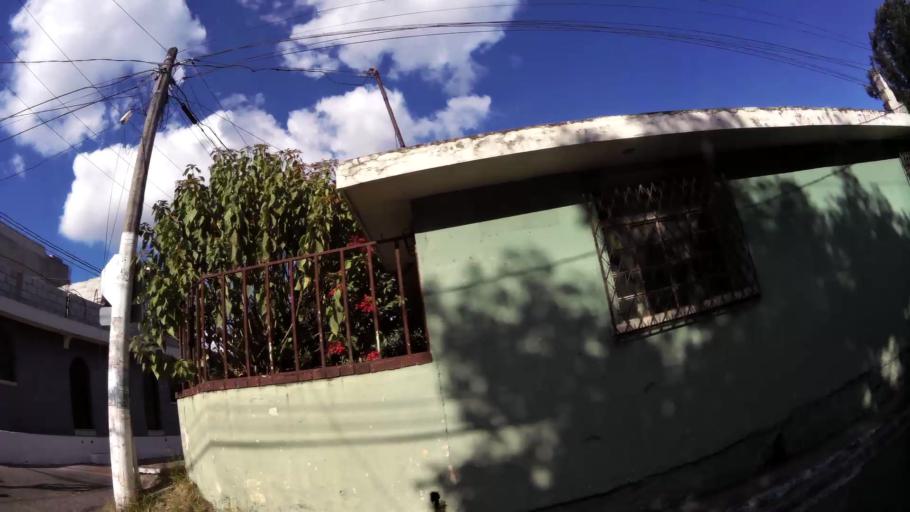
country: GT
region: Guatemala
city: Villa Nueva
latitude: 14.5252
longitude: -90.5838
